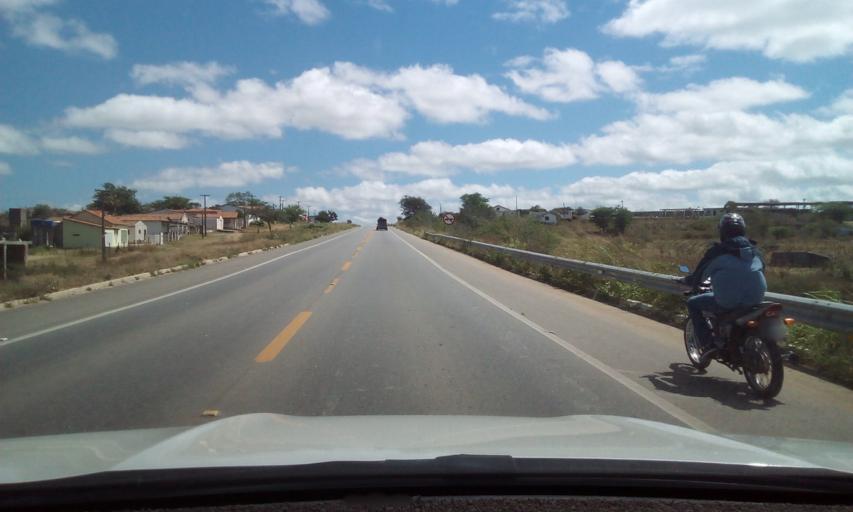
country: BR
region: Paraiba
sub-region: Campina Grande
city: Campina Grande
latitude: -7.3418
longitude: -35.8994
